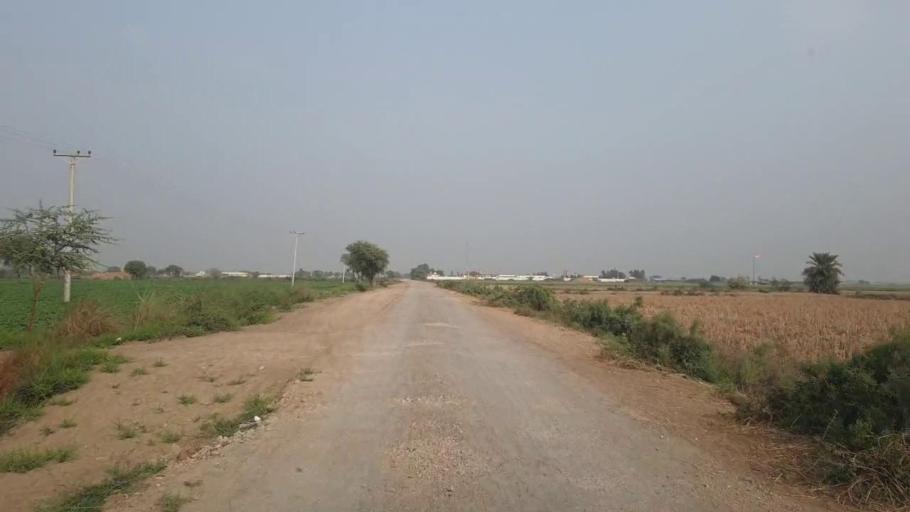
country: PK
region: Sindh
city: Mirpur Batoro
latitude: 24.5672
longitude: 68.4063
